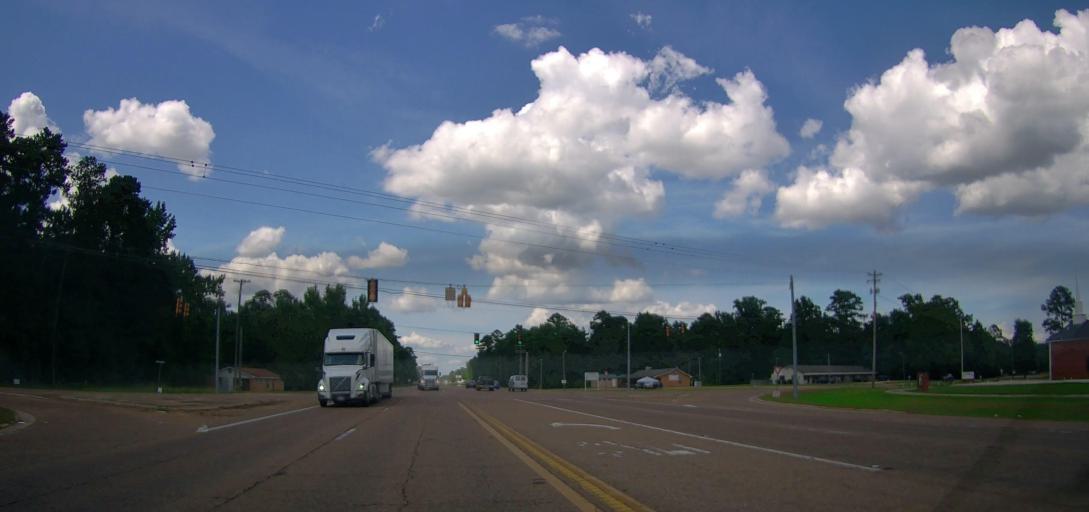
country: US
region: Mississippi
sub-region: Lowndes County
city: Columbus Air Force Base
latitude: 33.5813
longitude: -88.4285
